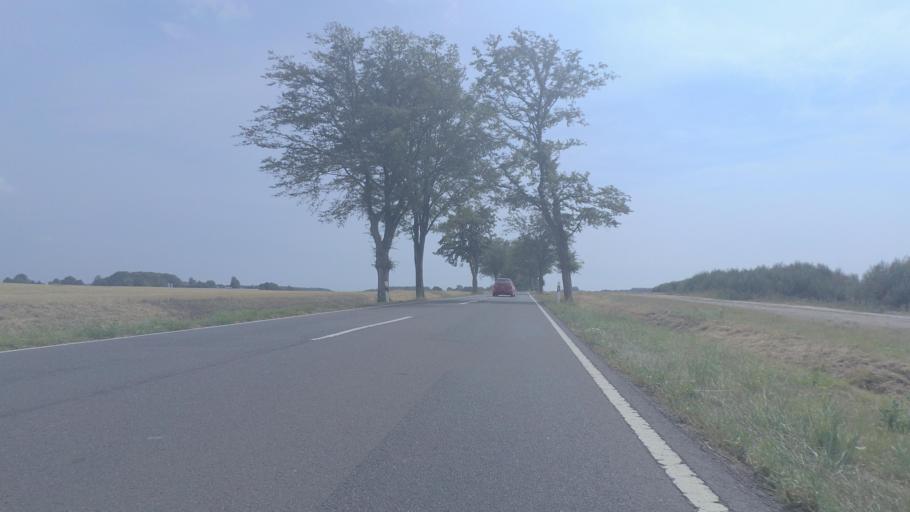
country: DE
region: Mecklenburg-Vorpommern
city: Samtens
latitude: 54.3440
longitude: 13.3079
